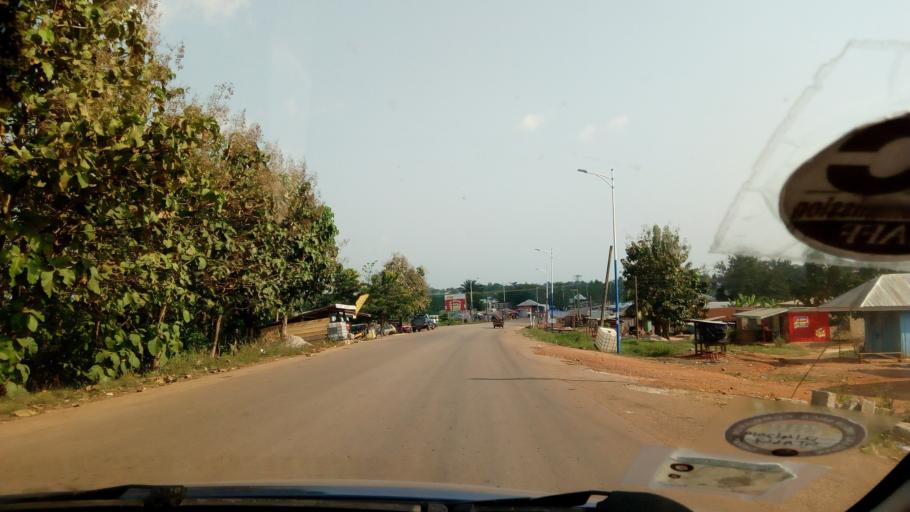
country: GH
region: Western
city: Bibiani
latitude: 6.7988
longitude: -2.5189
